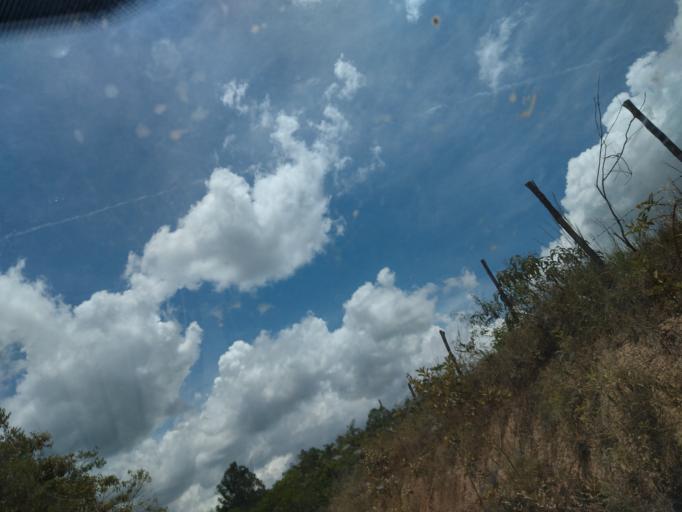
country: BR
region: Minas Gerais
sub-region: Sao Joao Del Rei
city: Sao Joao del Rei
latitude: -20.8993
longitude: -44.3027
